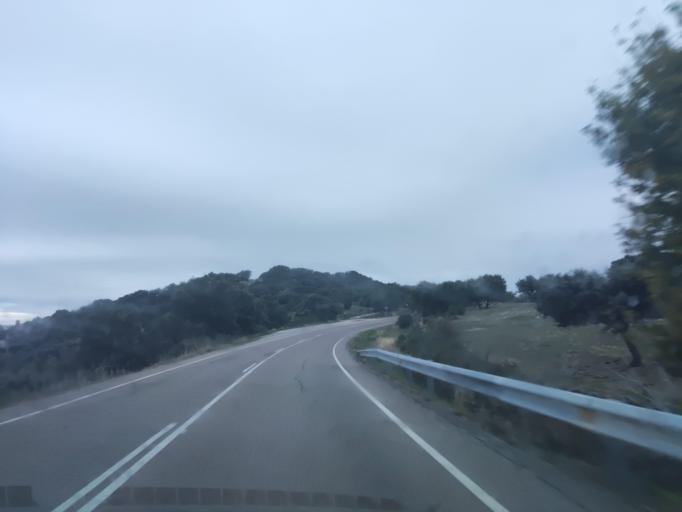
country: ES
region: Castille and Leon
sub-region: Provincia de Salamanca
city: Hinojosa de Duero
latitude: 40.9742
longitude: -6.8351
